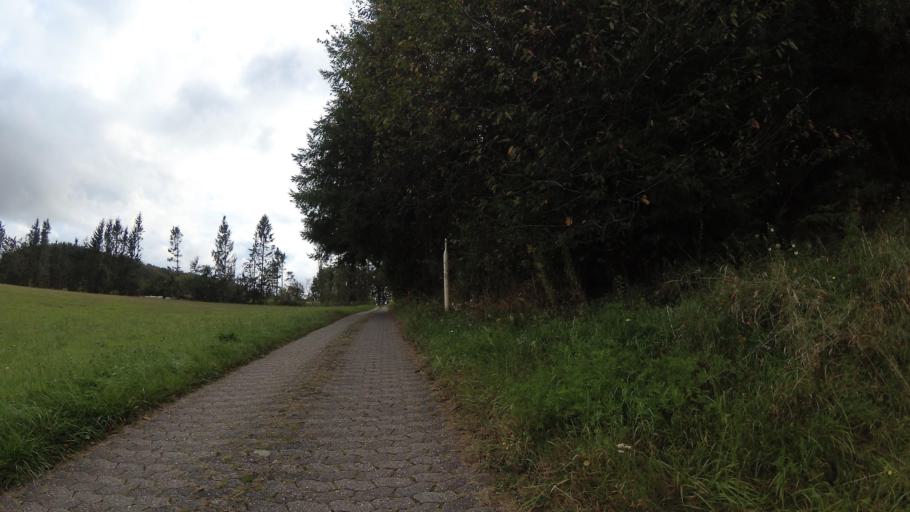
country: DE
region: Rheinland-Pfalz
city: Reichweiler
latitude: 49.5297
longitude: 7.2801
